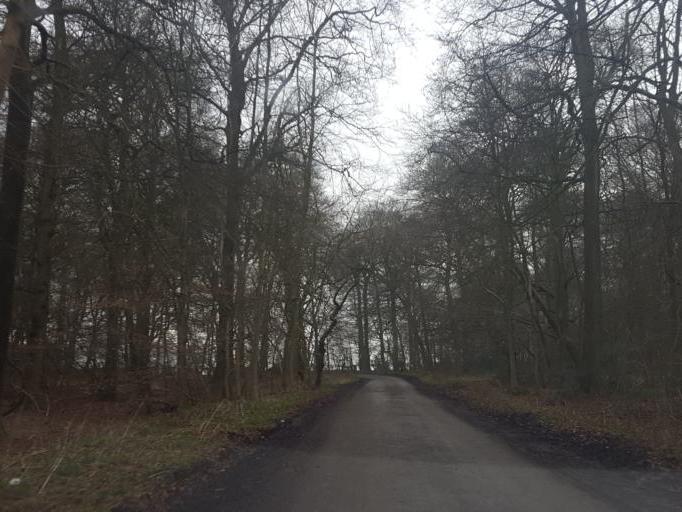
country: GB
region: England
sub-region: Buckinghamshire
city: Stokenchurch
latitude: 51.6646
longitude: -0.9375
